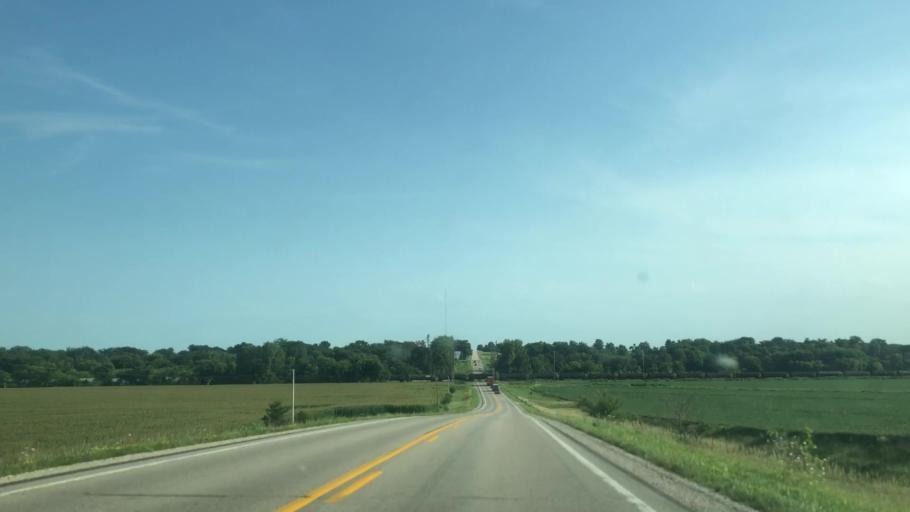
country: US
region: Iowa
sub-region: Marshall County
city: Marshalltown
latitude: 42.0339
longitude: -93.0000
